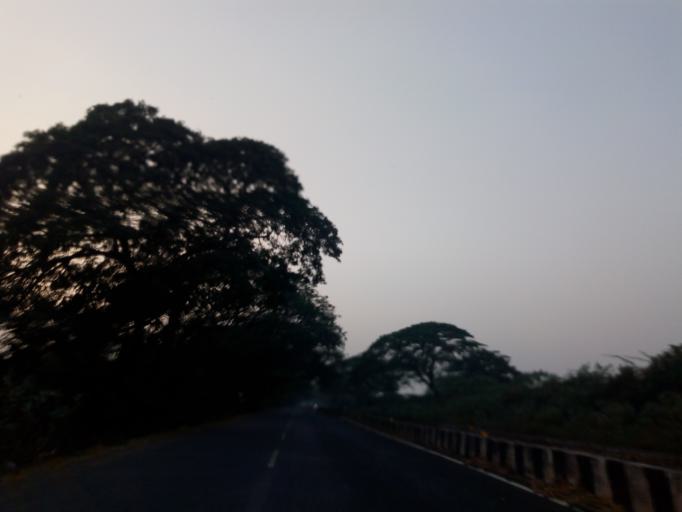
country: IN
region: Andhra Pradesh
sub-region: West Godavari
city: Tadepallegudem
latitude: 16.8148
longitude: 81.5017
